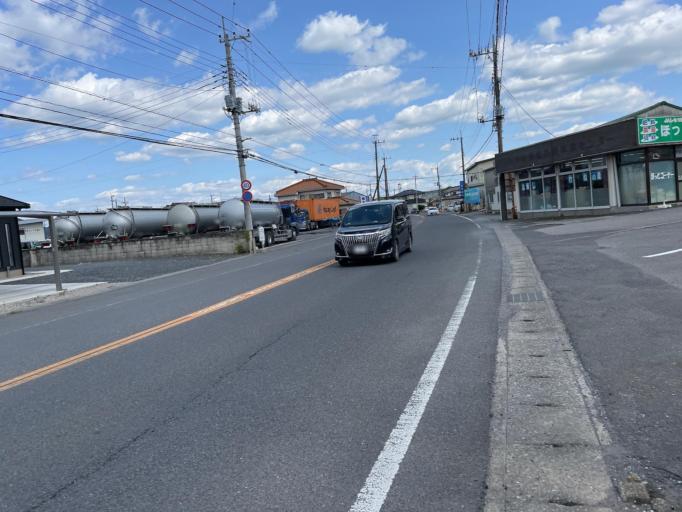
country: JP
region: Tochigi
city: Sano
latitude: 36.3194
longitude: 139.6434
